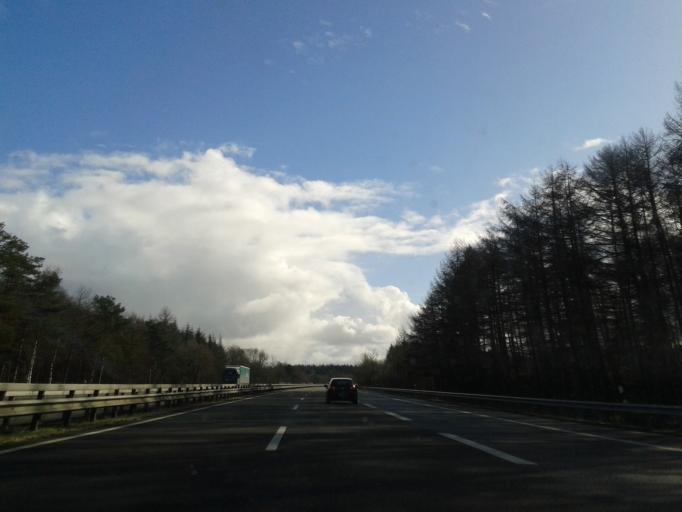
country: DE
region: Lower Saxony
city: Bad Zwischenahn
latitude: 53.2467
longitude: 8.0111
